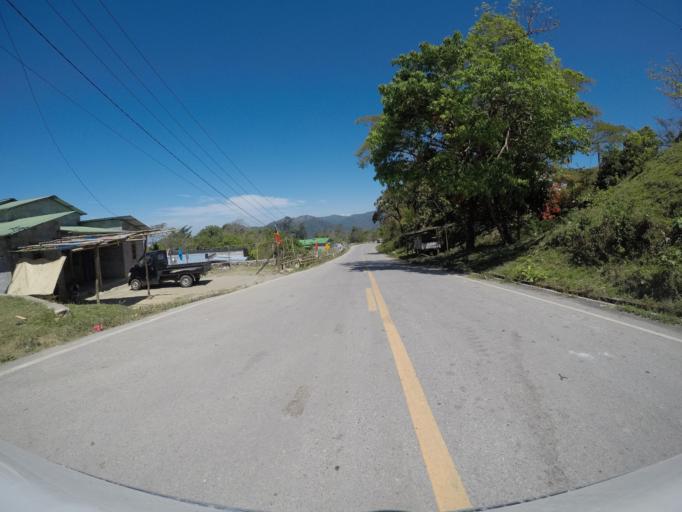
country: TL
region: Manatuto
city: Manatuto
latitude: -8.8255
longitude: 125.9832
